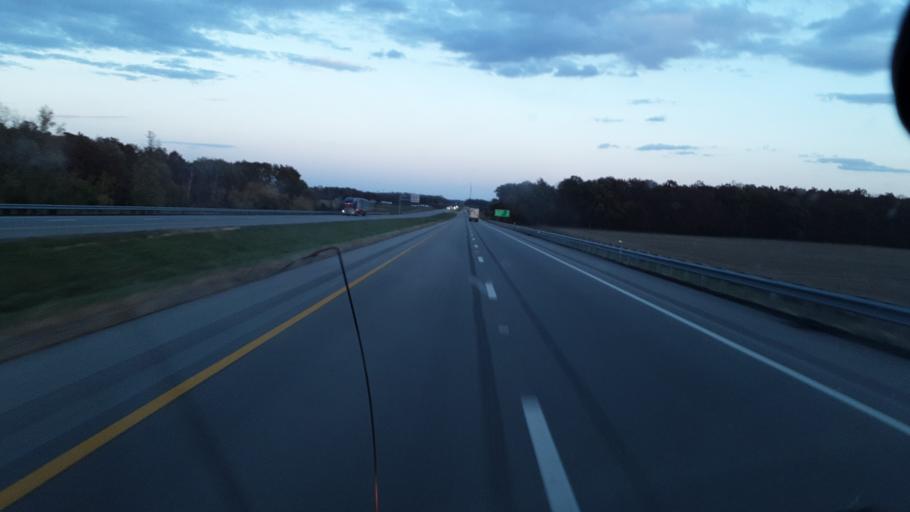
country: US
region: Ohio
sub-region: Williams County
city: Pioneer
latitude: 41.6115
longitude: -84.5305
